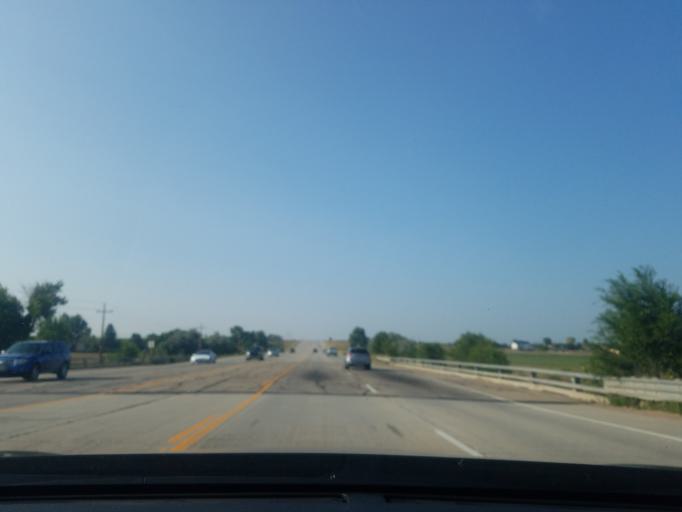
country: US
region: Colorado
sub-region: Larimer County
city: Berthoud
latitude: 40.2770
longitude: -105.1025
